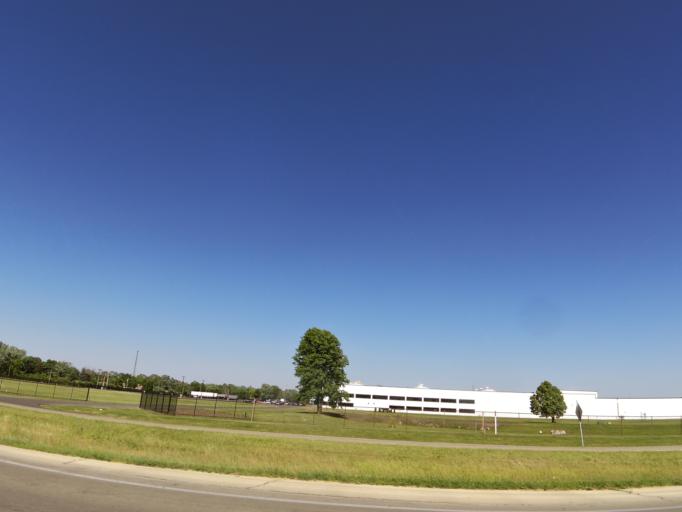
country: US
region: Illinois
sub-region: Winnebago County
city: Roscoe
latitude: 42.4405
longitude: -89.0175
